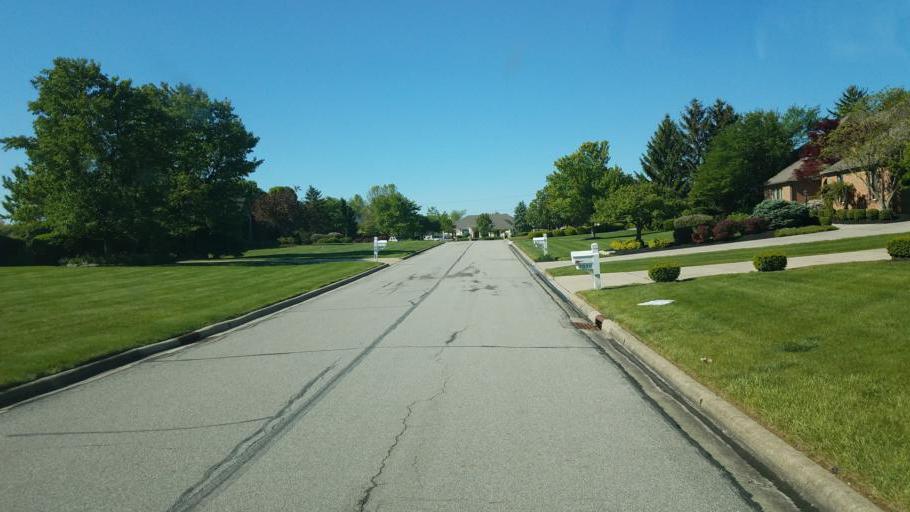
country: US
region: Ohio
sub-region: Franklin County
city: Westerville
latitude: 40.1604
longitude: -82.9419
